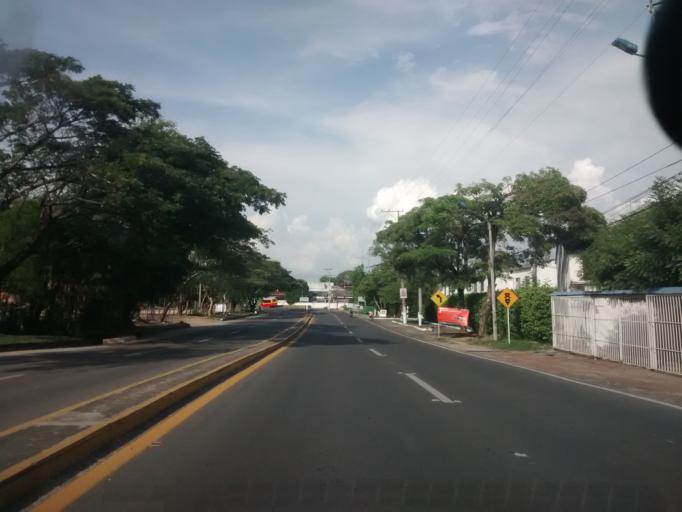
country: CO
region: Cundinamarca
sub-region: Girardot
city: Girardot City
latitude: 4.3180
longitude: -74.8036
